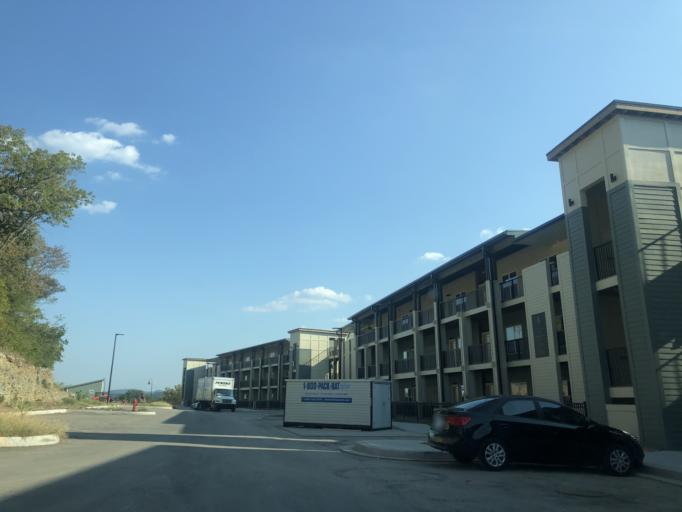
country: US
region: Tennessee
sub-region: Davidson County
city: Belle Meade
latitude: 36.1341
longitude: -86.9012
